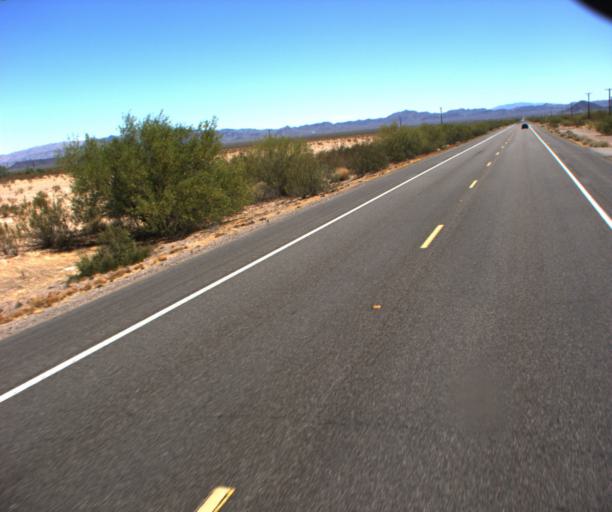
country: US
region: Arizona
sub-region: La Paz County
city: Salome
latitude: 33.7003
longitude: -113.8564
